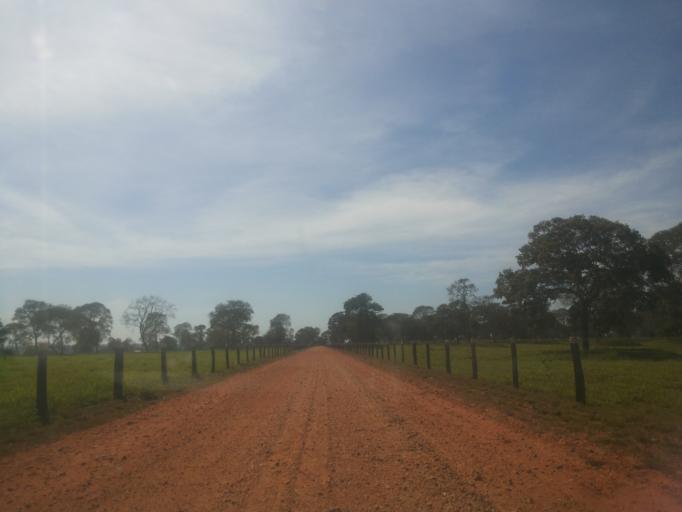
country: BR
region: Minas Gerais
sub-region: Santa Vitoria
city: Santa Vitoria
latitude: -19.0130
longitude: -50.4313
